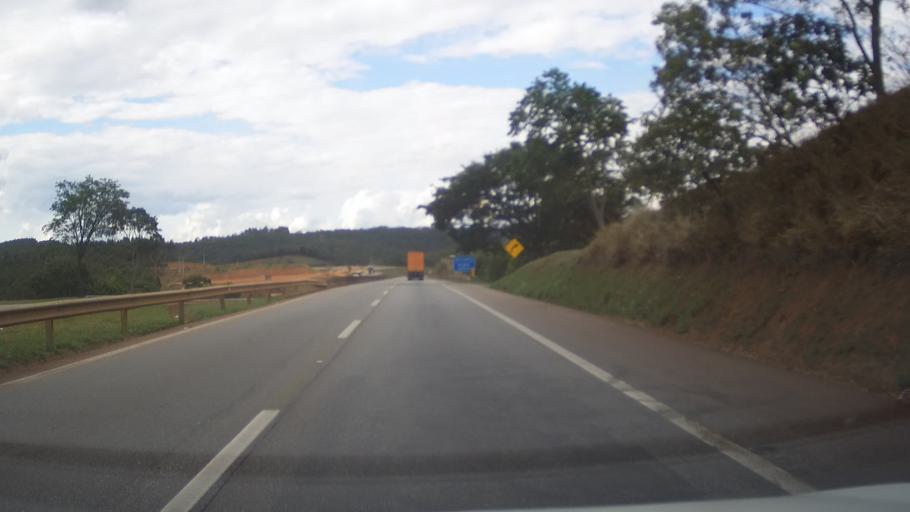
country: BR
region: Minas Gerais
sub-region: Itauna
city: Itauna
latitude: -20.2911
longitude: -44.4363
